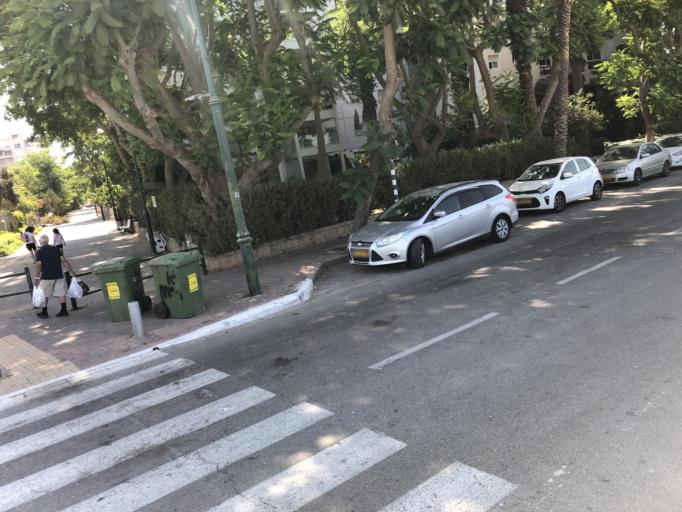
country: IL
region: Central District
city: Yehud
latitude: 32.0318
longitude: 34.8777
